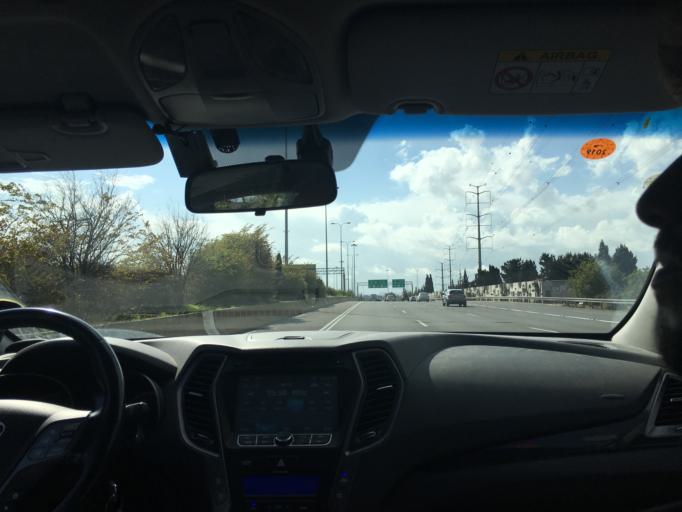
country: IL
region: Tel Aviv
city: Azor
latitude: 32.0447
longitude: 34.8297
